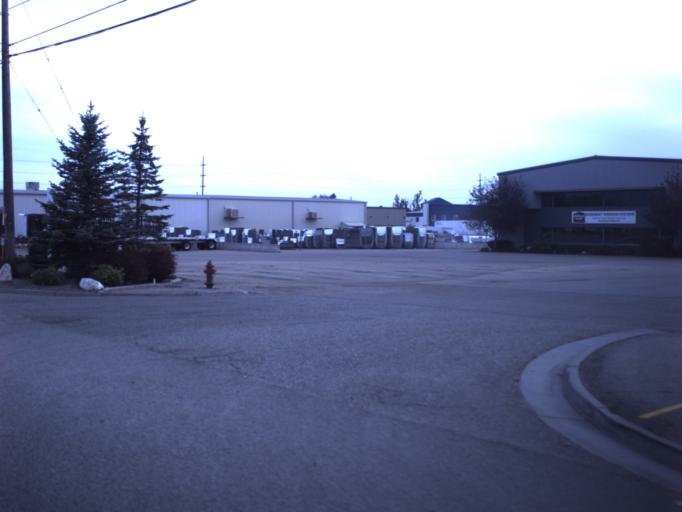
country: US
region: Utah
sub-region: Weber County
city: Marriott-Slaterville
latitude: 41.2219
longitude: -112.0258
